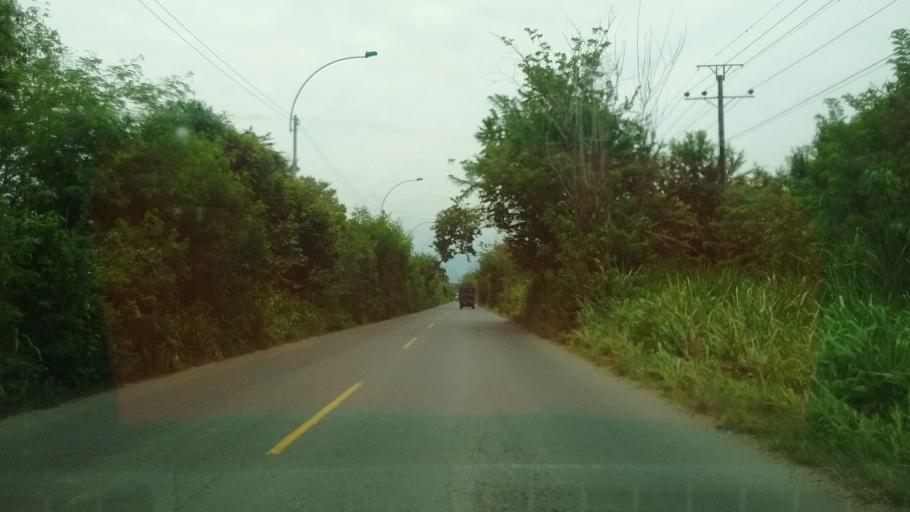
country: CO
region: Valle del Cauca
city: Jamundi
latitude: 3.3324
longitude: -76.5105
